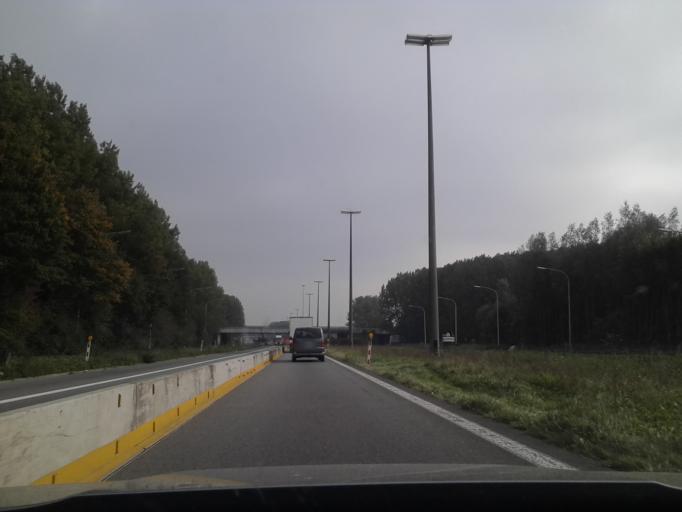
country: BE
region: Wallonia
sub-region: Province du Hainaut
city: Rumes
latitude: 50.6132
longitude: 3.3202
